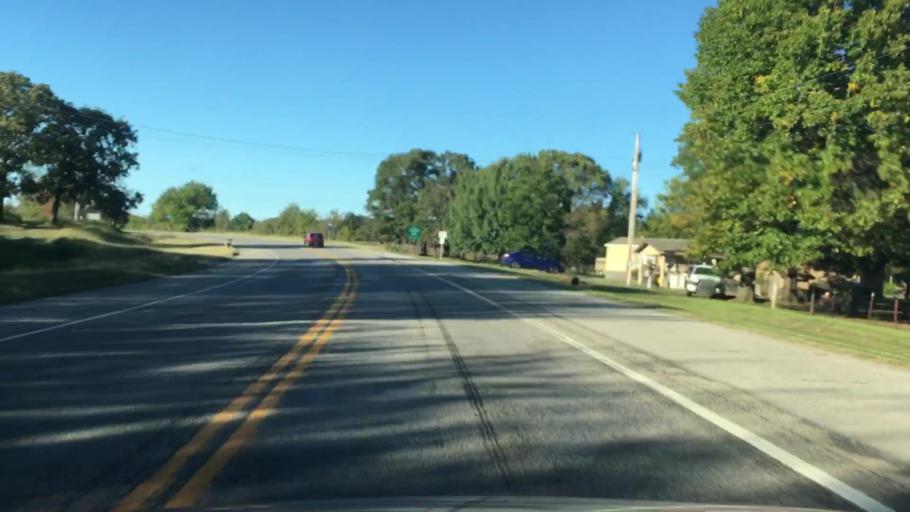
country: US
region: Oklahoma
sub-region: Cherokee County
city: Tahlequah
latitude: 35.9286
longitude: -95.1239
